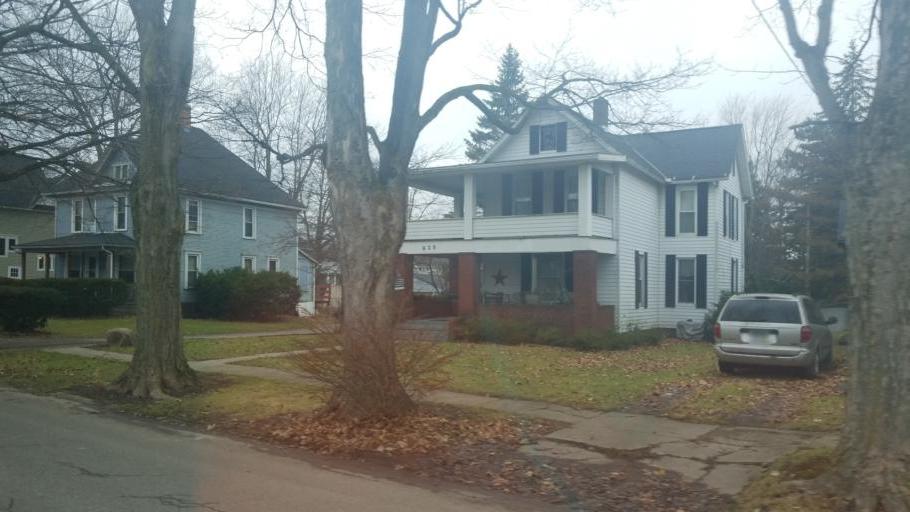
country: US
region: Ohio
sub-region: Crawford County
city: Galion
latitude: 40.7423
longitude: -82.7886
